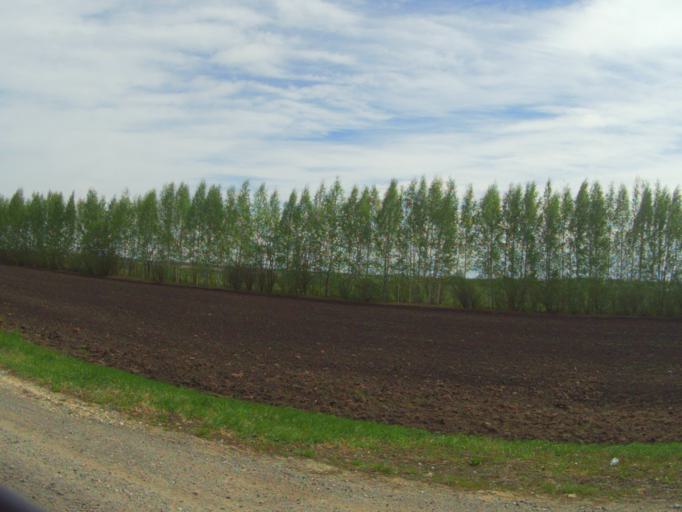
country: RU
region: Mordoviya
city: Chamzinka
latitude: 54.3482
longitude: 45.5678
